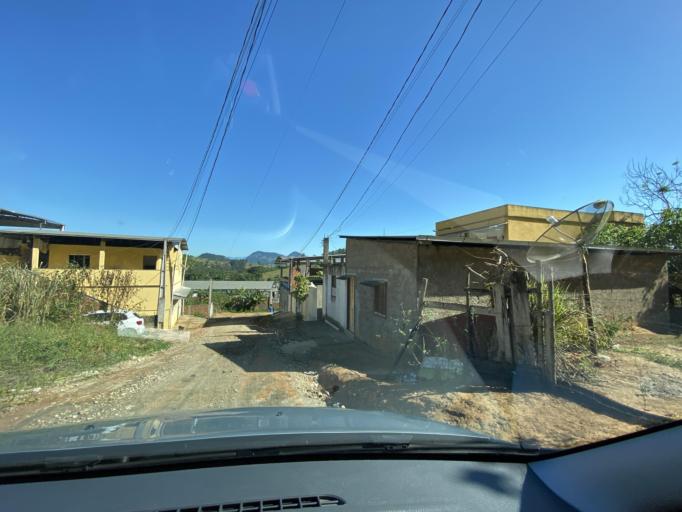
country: BR
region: Espirito Santo
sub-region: Jeronimo Monteiro
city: Jeronimo Monteiro
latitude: -20.7972
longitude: -41.4001
